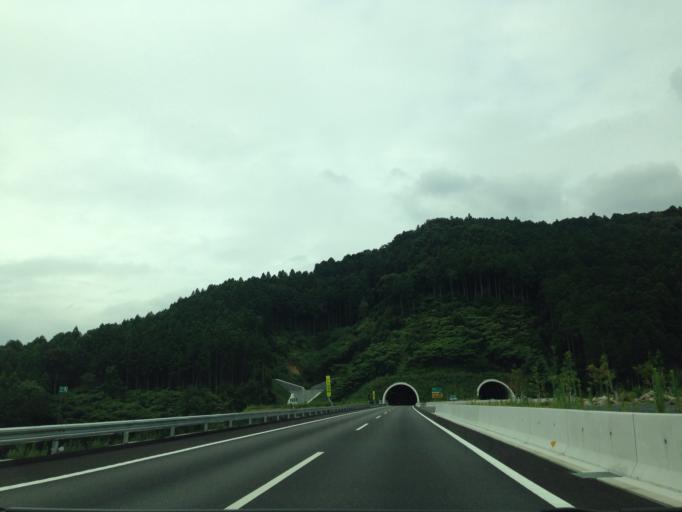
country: JP
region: Aichi
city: Shinshiro
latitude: 34.9183
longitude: 137.4898
